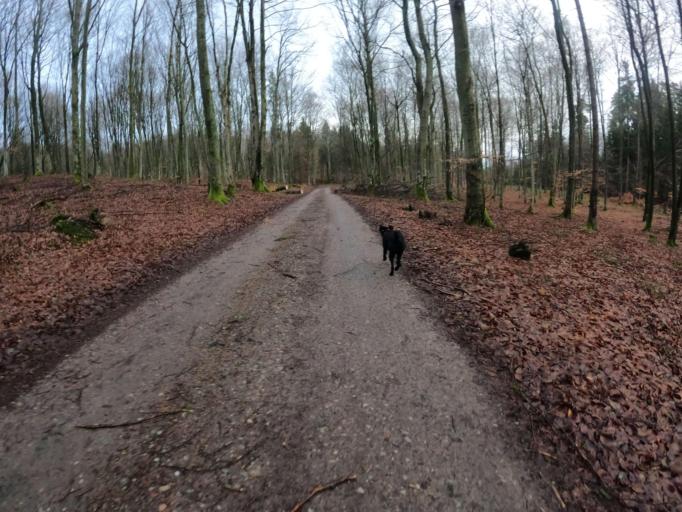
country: PL
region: West Pomeranian Voivodeship
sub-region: Powiat slawienski
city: Slawno
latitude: 54.2721
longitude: 16.7187
